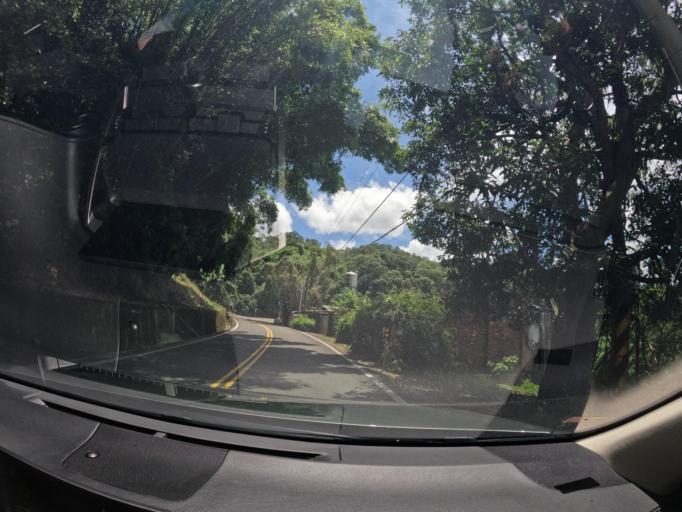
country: TW
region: Taiwan
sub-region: Hsinchu
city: Hsinchu
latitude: 24.6396
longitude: 120.9849
